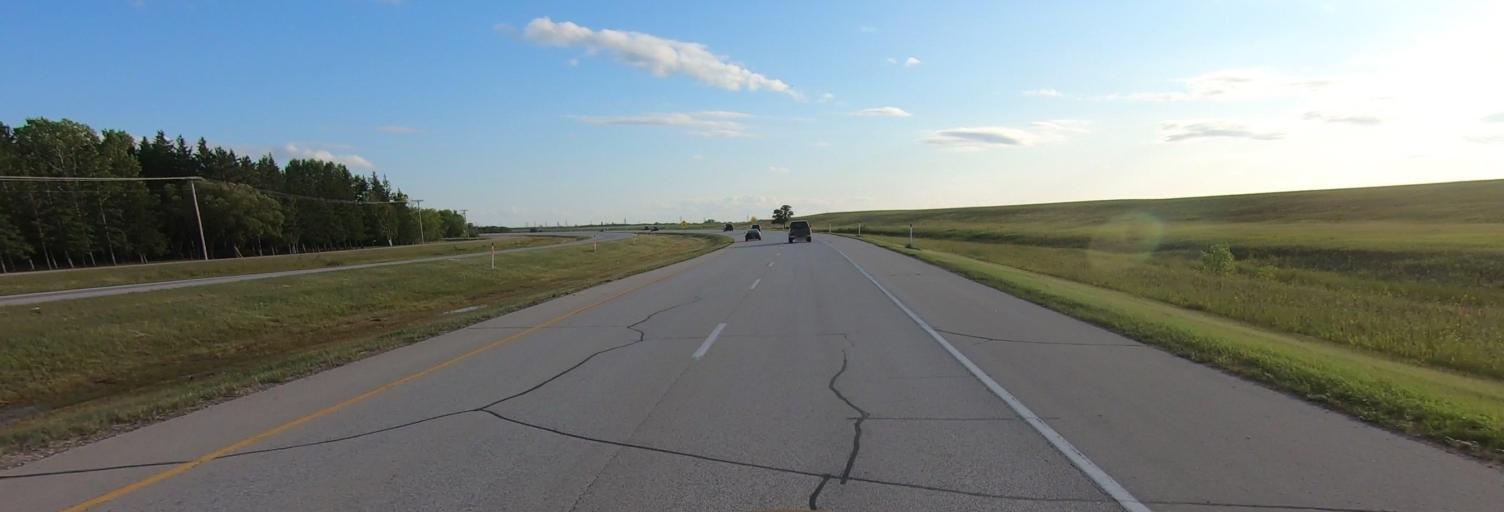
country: CA
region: Manitoba
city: Selkirk
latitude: 49.9941
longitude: -96.9747
